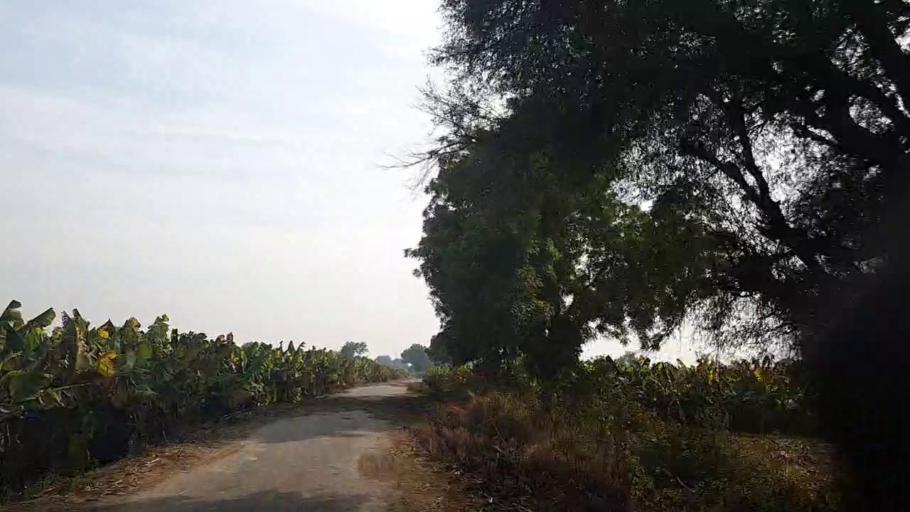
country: PK
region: Sindh
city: Daur
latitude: 26.3983
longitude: 68.2016
